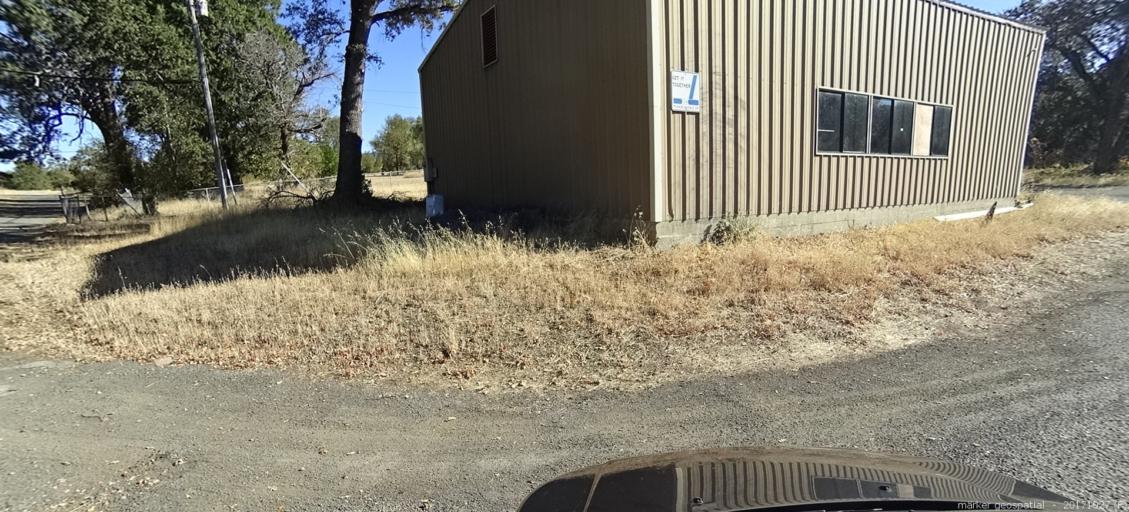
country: US
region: California
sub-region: Shasta County
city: Burney
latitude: 40.7931
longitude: -121.9408
